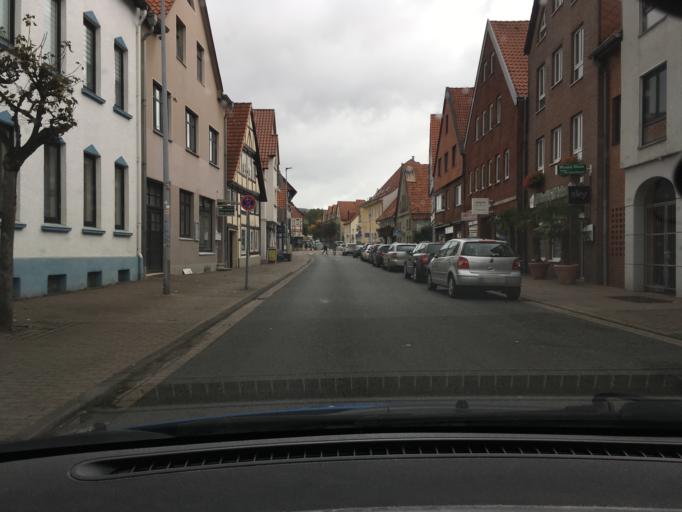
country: DE
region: Lower Saxony
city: Springe
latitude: 52.2080
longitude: 9.5555
